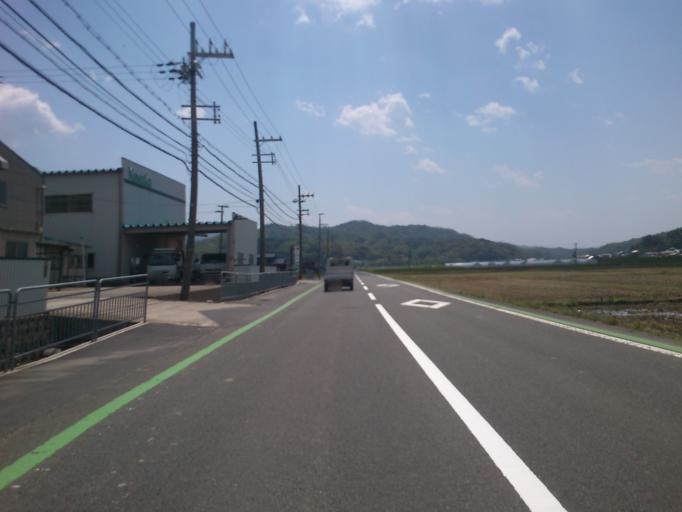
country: JP
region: Kyoto
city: Miyazu
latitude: 35.7248
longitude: 135.1067
